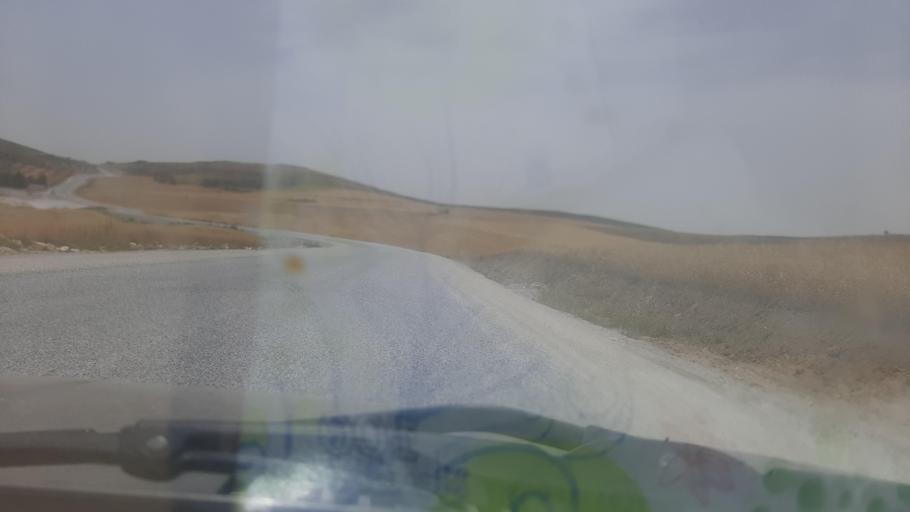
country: TN
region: Tunis
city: La Mohammedia
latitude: 36.5405
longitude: 10.1521
